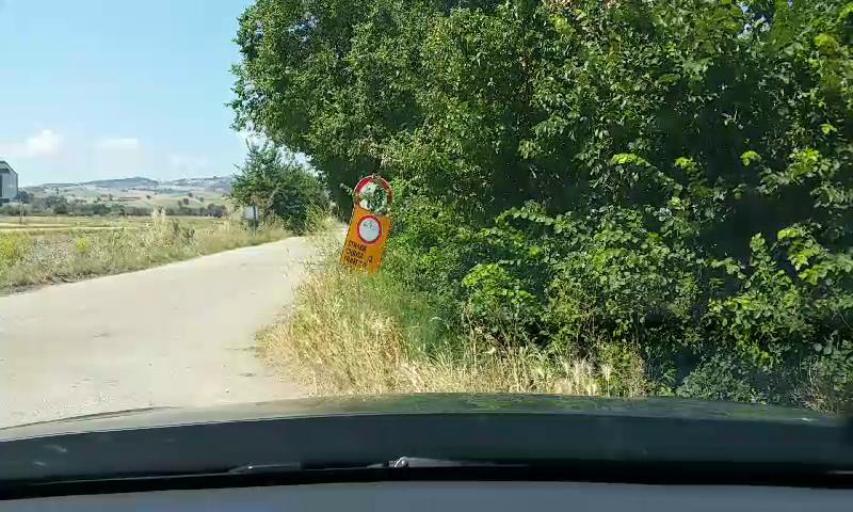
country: IT
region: Molise
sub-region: Provincia di Campobasso
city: Guglionesi
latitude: 41.9391
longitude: 14.8926
